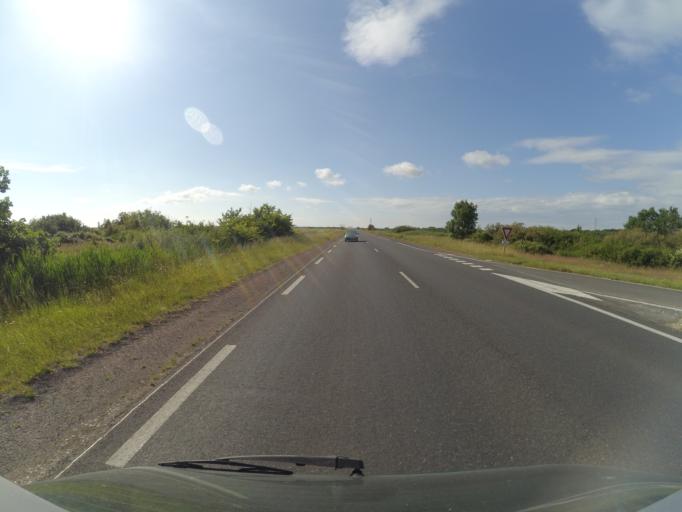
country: FR
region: Poitou-Charentes
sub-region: Departement de la Charente-Maritime
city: Saint-Agnant
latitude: 45.8487
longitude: -0.9554
